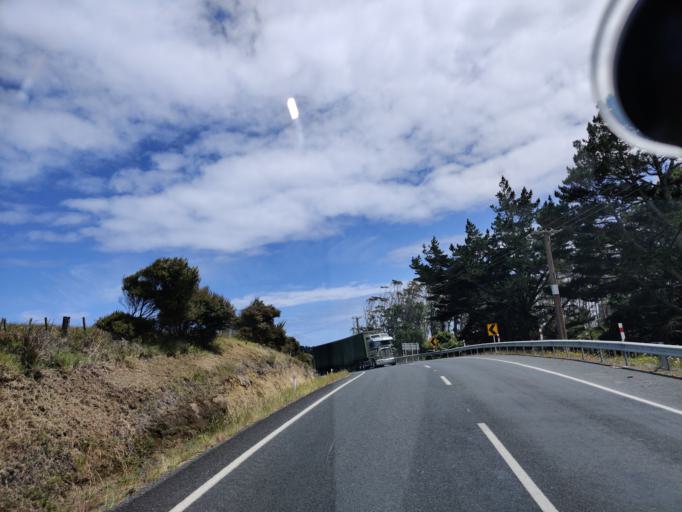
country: NZ
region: Northland
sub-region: Far North District
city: Kaitaia
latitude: -35.0114
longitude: 173.2072
